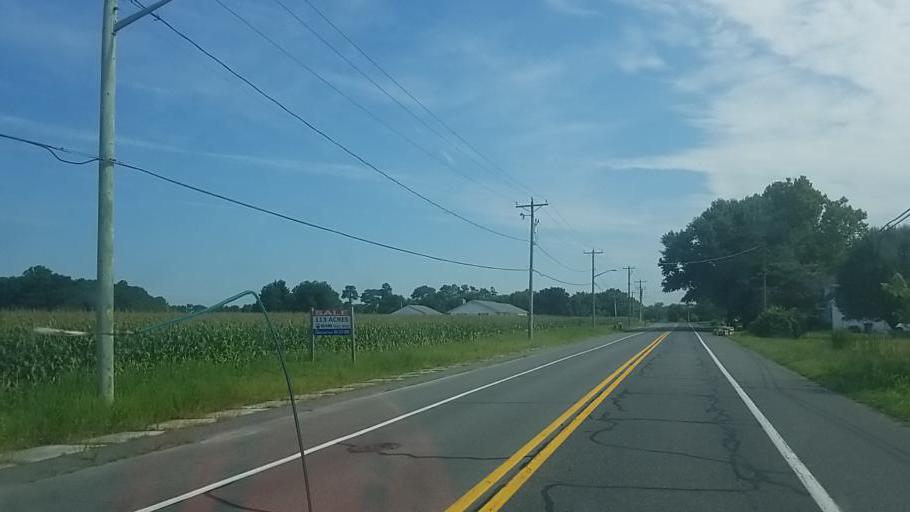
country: US
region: Delaware
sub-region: Sussex County
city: Selbyville
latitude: 38.5276
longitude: -75.2370
